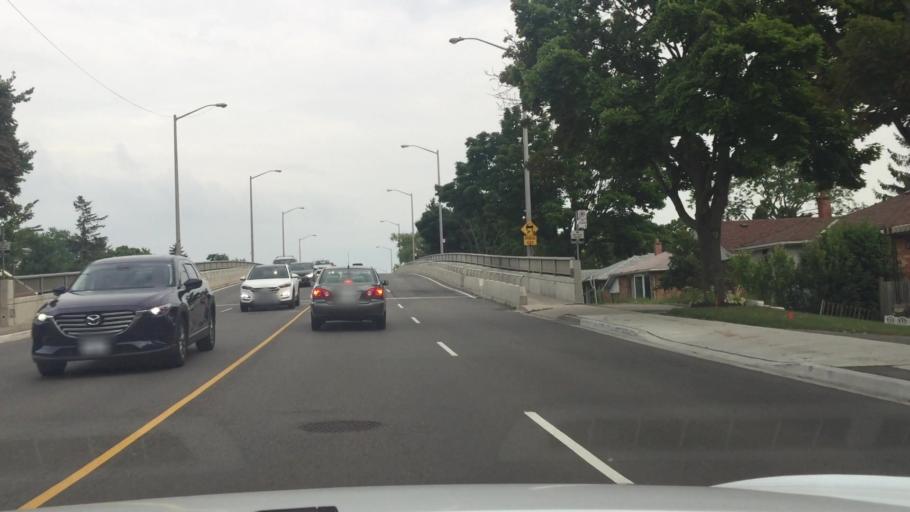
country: CA
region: Ontario
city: Scarborough
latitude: 43.7516
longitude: -79.3080
